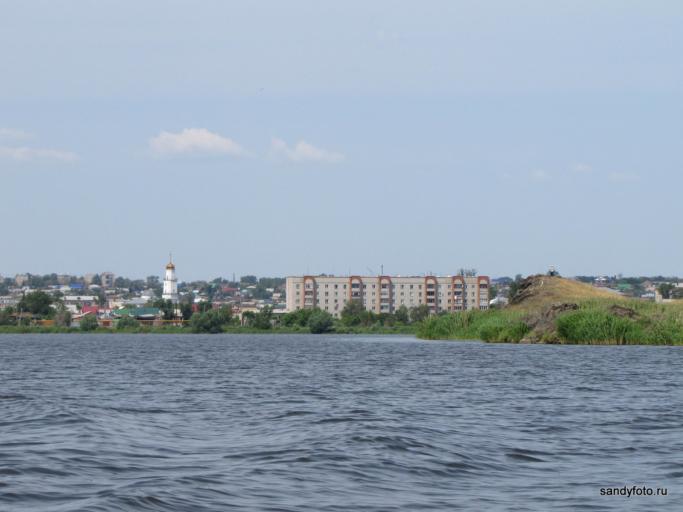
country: RU
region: Chelyabinsk
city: Troitsk
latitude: 54.0739
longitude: 61.5786
